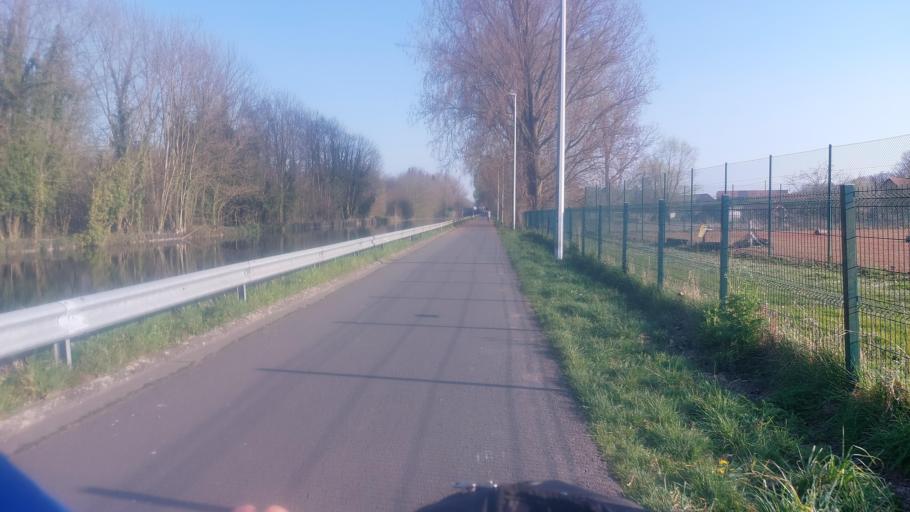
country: BE
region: Wallonia
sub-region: Province du Hainaut
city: Ath
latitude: 50.6237
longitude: 3.7834
